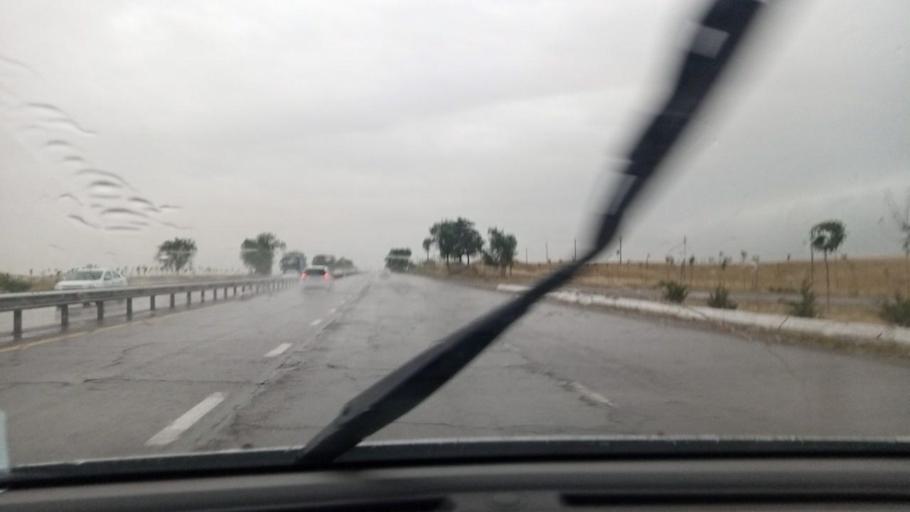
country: UZ
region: Toshkent
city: Ohangaron
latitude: 40.9881
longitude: 69.5351
